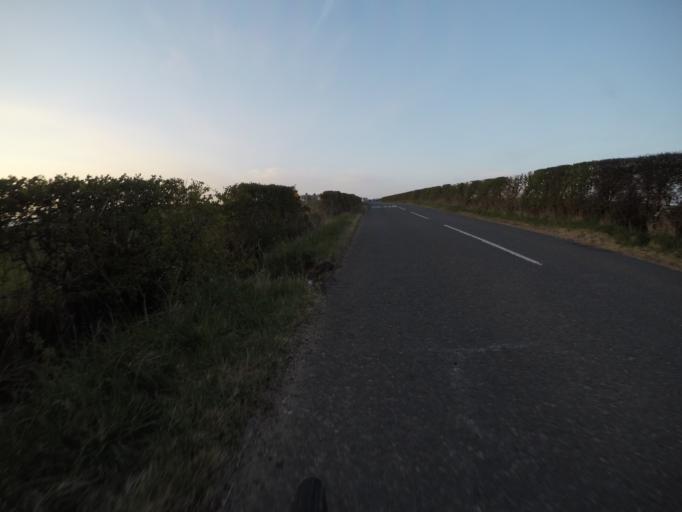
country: GB
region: Scotland
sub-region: South Ayrshire
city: Dundonald
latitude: 55.5580
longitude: -4.6123
